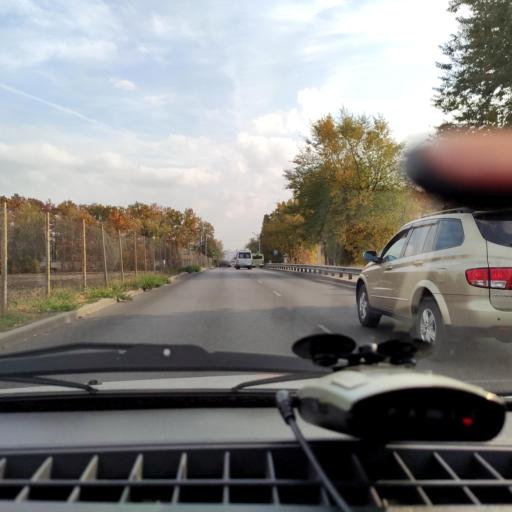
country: RU
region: Voronezj
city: Voronezh
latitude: 51.7054
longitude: 39.2282
